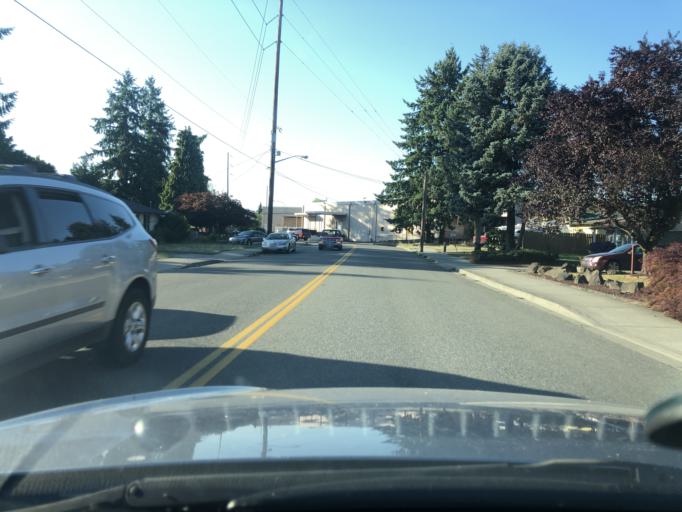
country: US
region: Washington
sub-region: King County
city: Auburn
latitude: 47.2913
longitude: -122.2129
